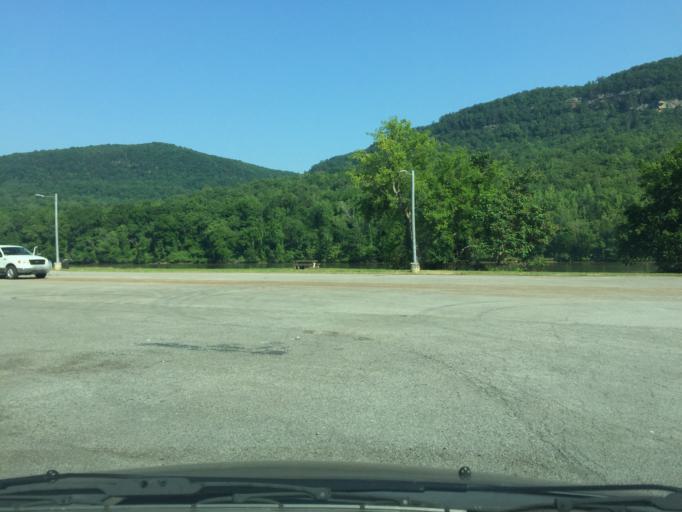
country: US
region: Tennessee
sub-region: Hamilton County
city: Lookout Mountain
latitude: 35.0600
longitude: -85.4156
